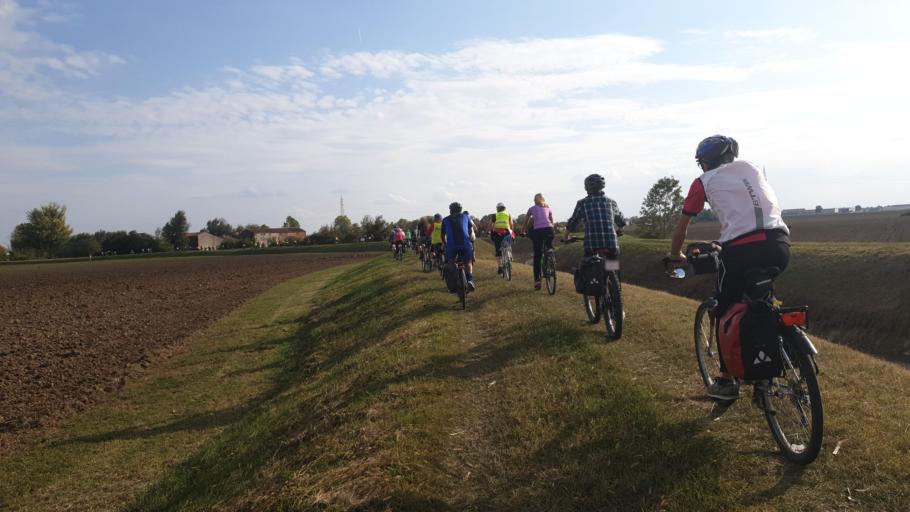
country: IT
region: Veneto
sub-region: Provincia di Vicenza
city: Poiana Maggiore
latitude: 45.2853
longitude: 11.4883
